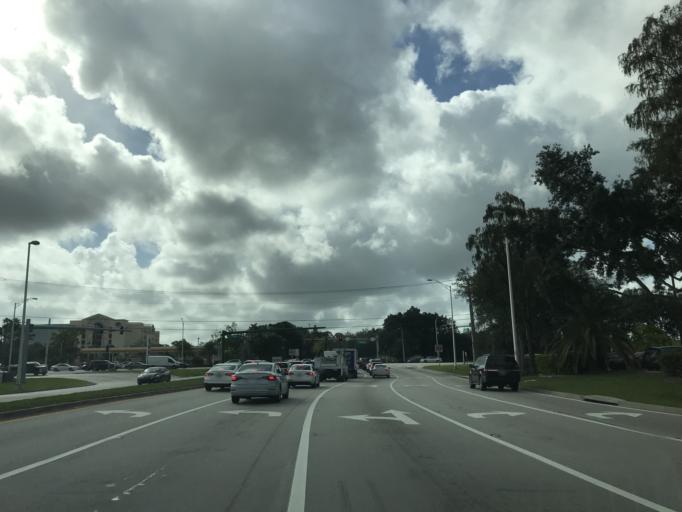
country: US
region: Florida
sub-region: Palm Beach County
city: Boca Del Mar
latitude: 26.3691
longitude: -80.1691
